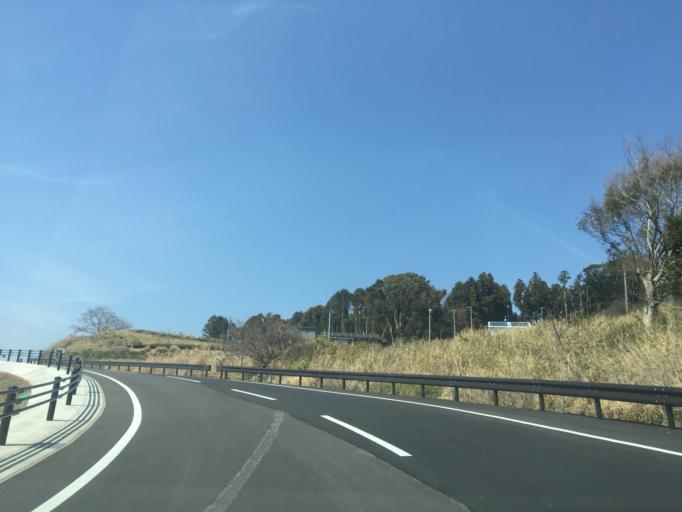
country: JP
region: Shizuoka
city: Kanaya
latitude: 34.8068
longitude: 138.1250
